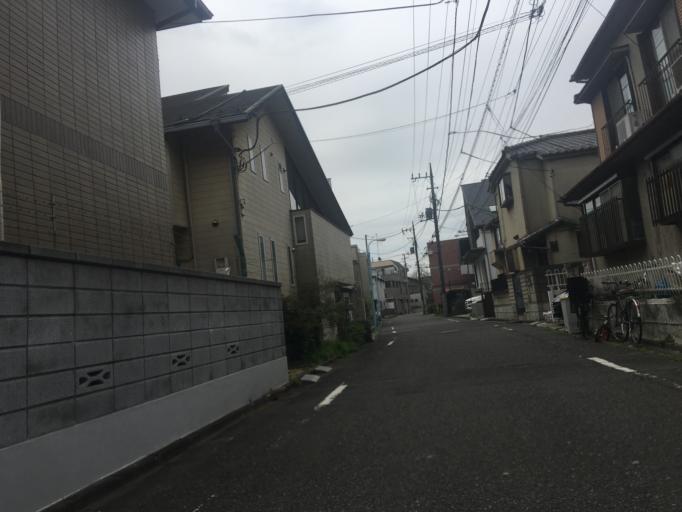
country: JP
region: Tokyo
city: Tokyo
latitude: 35.6787
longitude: 139.6506
